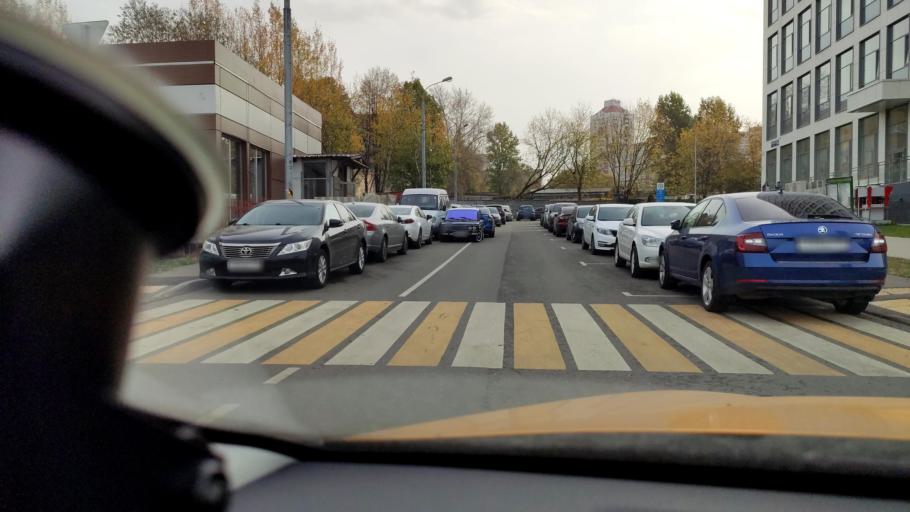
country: RU
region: Moskovskaya
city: Kastanayevo
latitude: 55.7088
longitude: 37.4985
